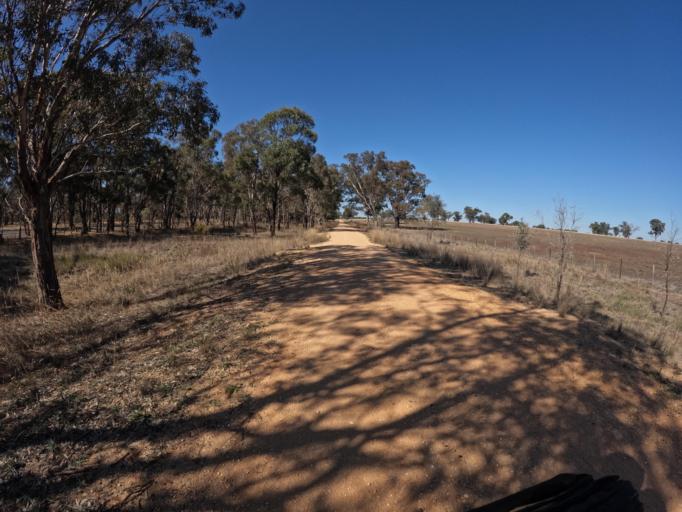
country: AU
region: Victoria
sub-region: Greater Bendigo
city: Kennington
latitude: -36.8332
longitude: 144.5943
